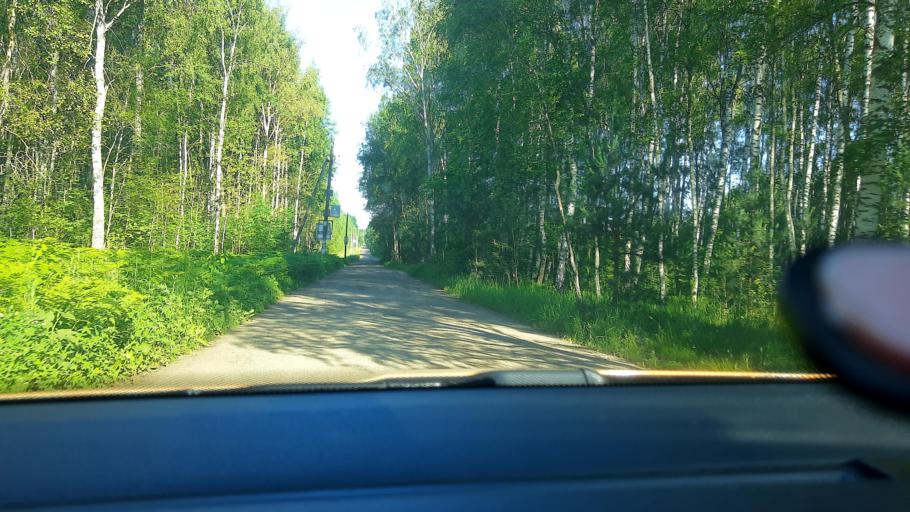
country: RU
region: Moskovskaya
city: Elektrogorsk
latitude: 55.8973
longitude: 38.7134
